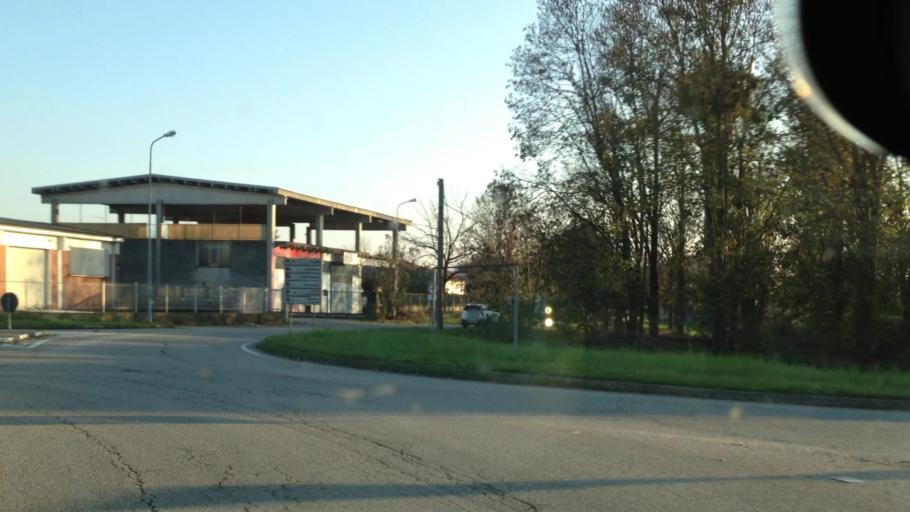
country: IT
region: Piedmont
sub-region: Provincia di Vercelli
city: Crescentino
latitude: 45.1978
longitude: 8.1035
